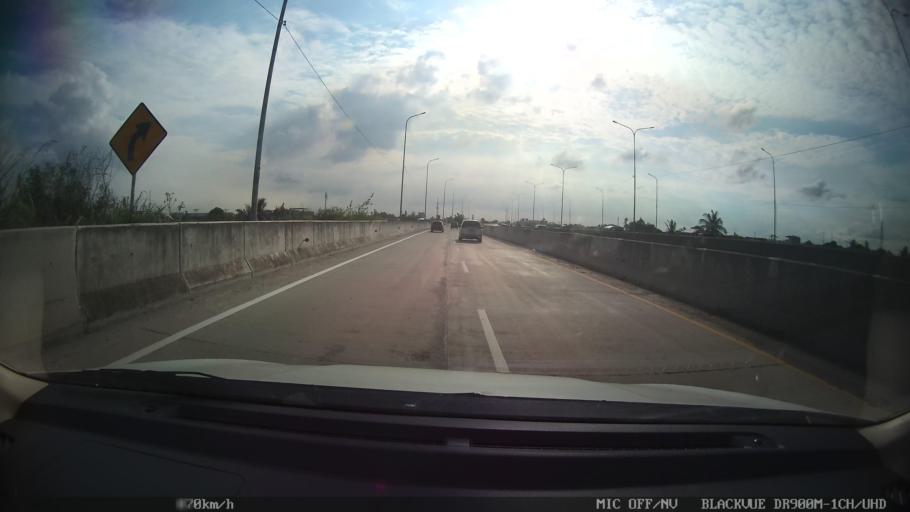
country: ID
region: North Sumatra
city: Medan
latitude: 3.6479
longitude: 98.6761
